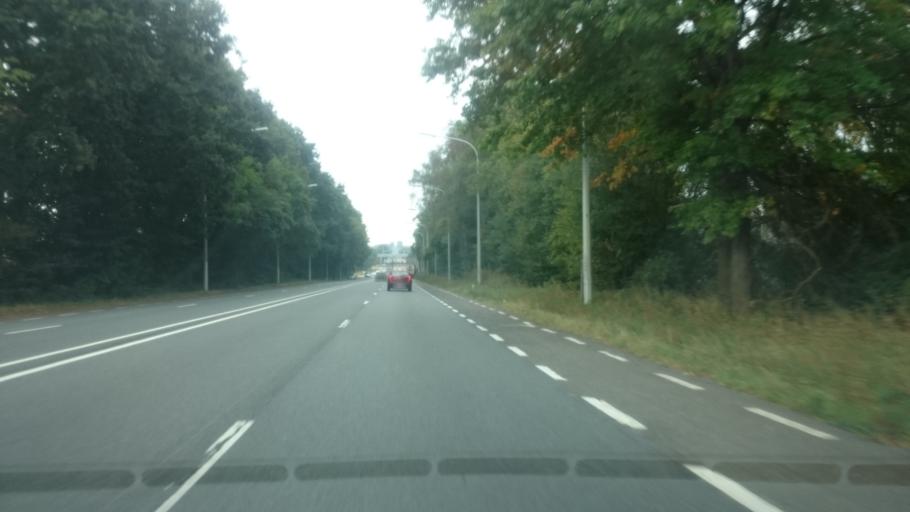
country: BE
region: Wallonia
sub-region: Province de Namur
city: Floreffe
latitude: 50.4883
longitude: 4.7917
